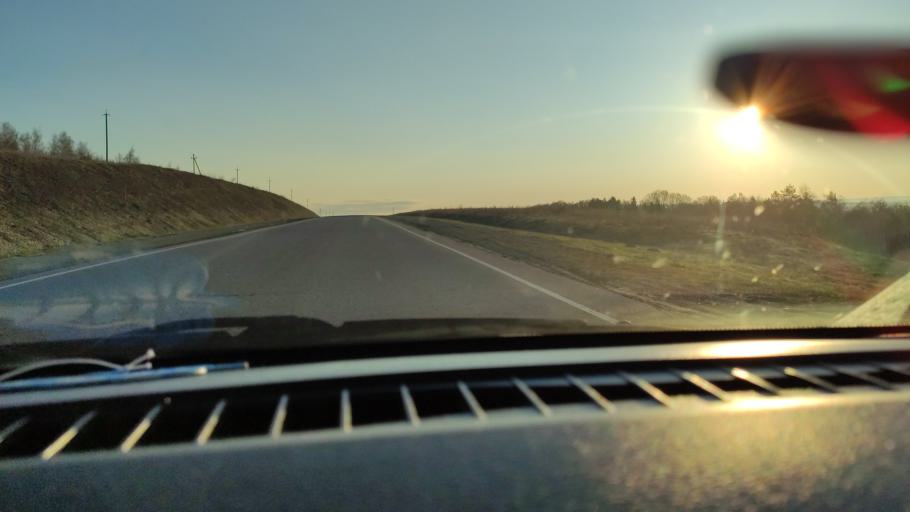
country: RU
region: Saratov
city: Sinodskoye
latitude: 52.0701
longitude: 46.7764
